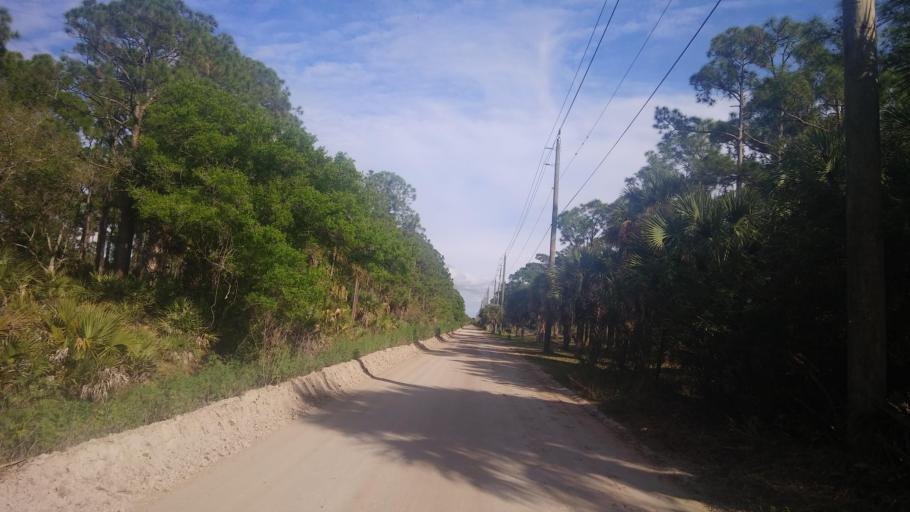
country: US
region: Florida
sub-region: Indian River County
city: Fellsmere
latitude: 27.7500
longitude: -80.5894
